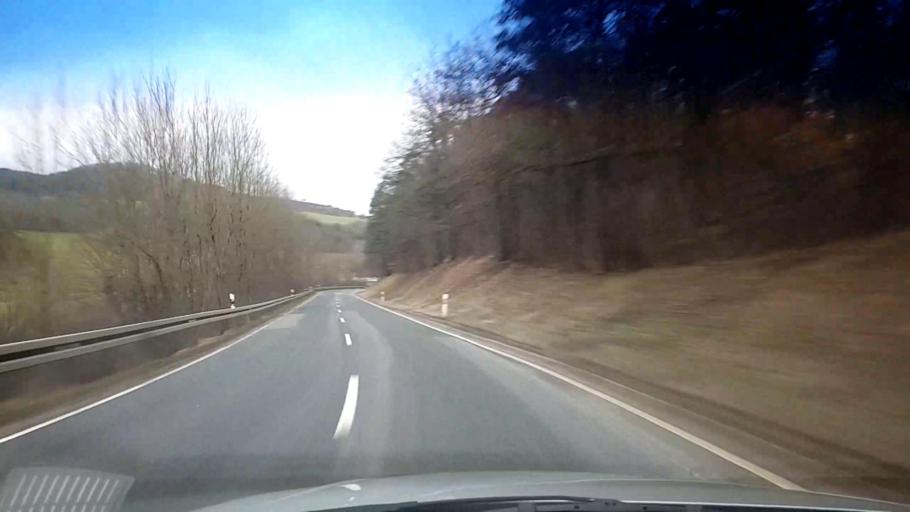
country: DE
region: Bavaria
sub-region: Upper Franconia
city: Wattendorf
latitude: 50.0548
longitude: 11.0787
